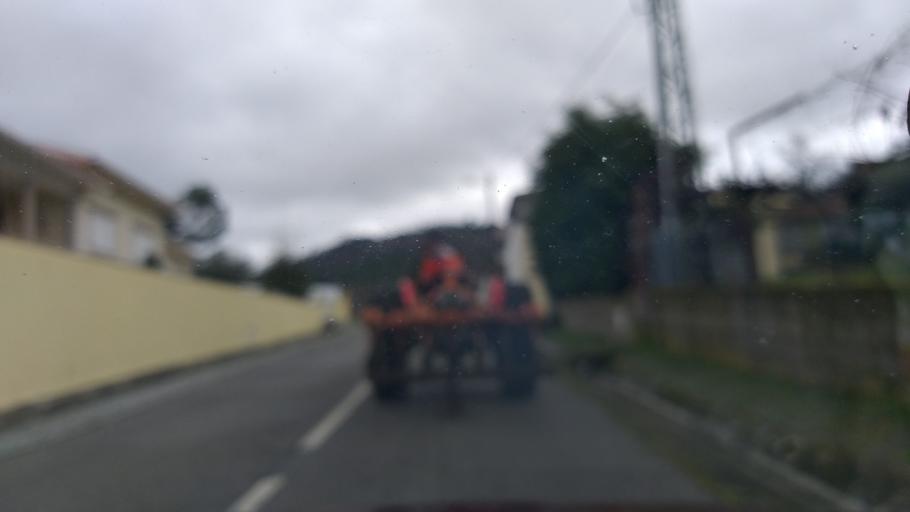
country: PT
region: Guarda
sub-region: Celorico da Beira
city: Celorico da Beira
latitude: 40.7103
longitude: -7.4342
